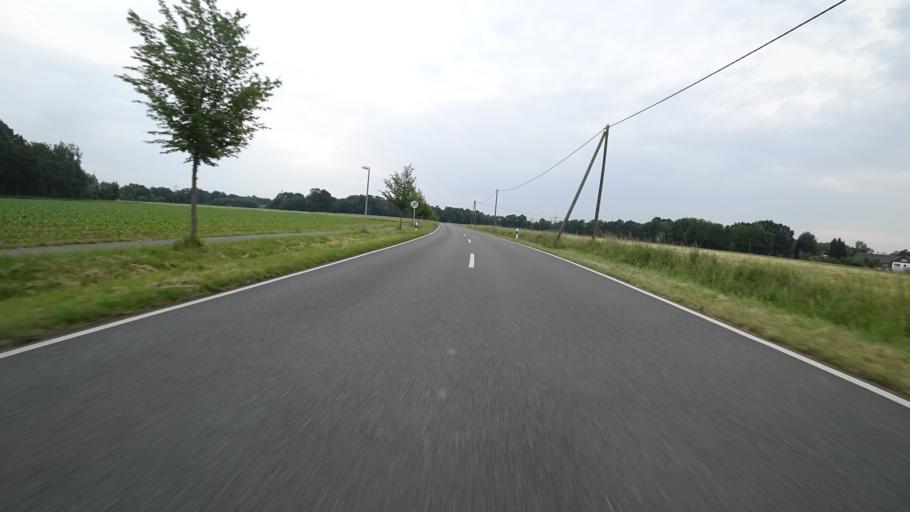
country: DE
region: North Rhine-Westphalia
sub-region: Regierungsbezirk Detmold
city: Guetersloh
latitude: 51.9404
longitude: 8.3799
